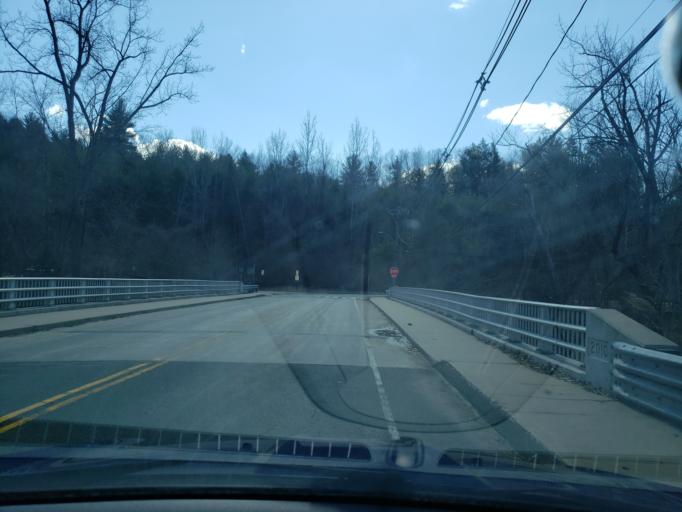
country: US
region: Connecticut
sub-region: Hartford County
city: Hazardville
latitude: 41.9820
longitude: -72.5400
